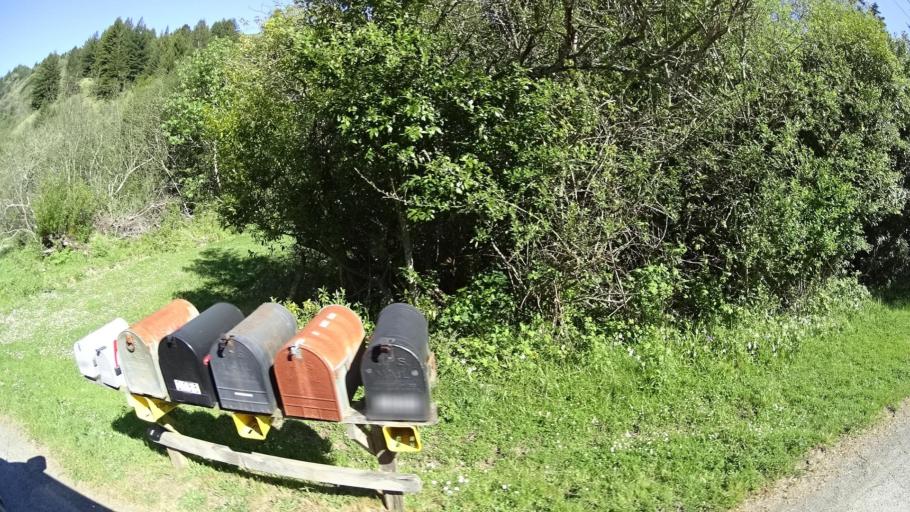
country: US
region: California
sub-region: Humboldt County
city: Fortuna
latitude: 40.5267
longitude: -124.1872
